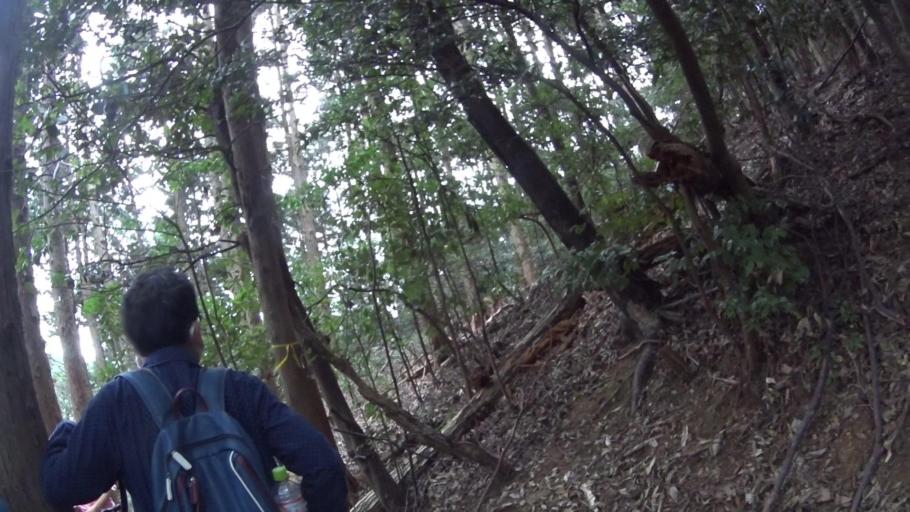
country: JP
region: Osaka
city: Kaizuka
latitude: 34.4719
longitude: 135.3044
